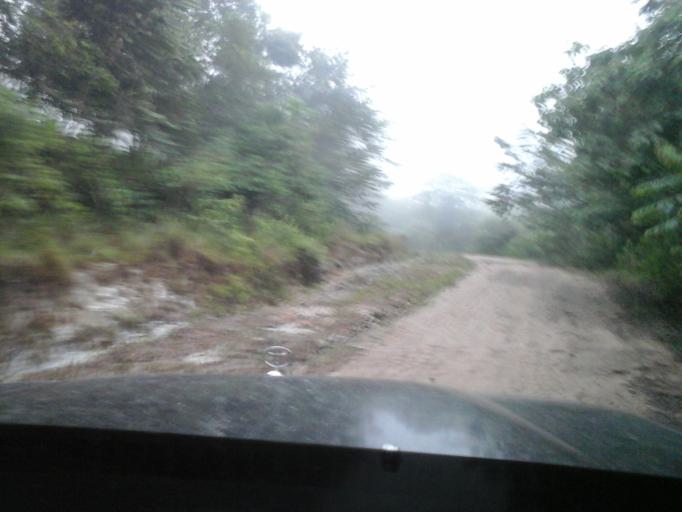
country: CO
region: Cesar
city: Agustin Codazzi
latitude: 9.9399
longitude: -73.1439
